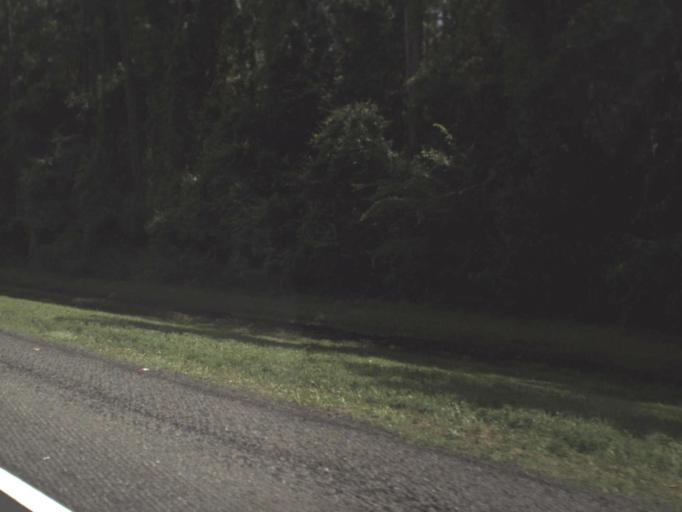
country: US
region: Florida
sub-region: Nassau County
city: Yulee
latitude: 30.4979
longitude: -81.6383
